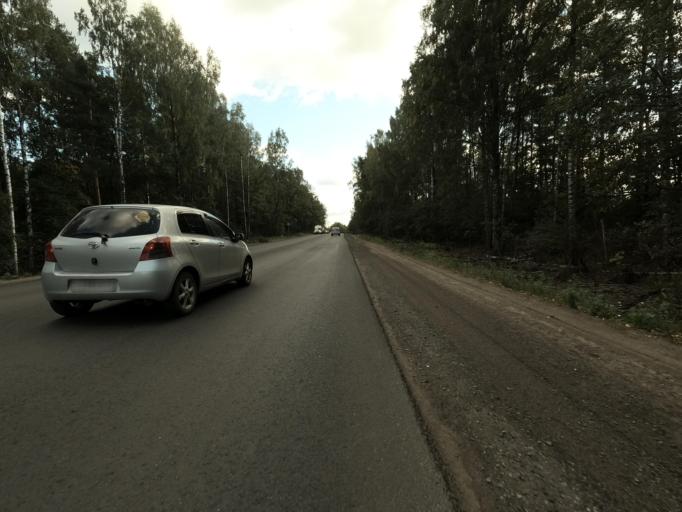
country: RU
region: Leningrad
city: Koltushi
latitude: 59.9518
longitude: 30.6567
